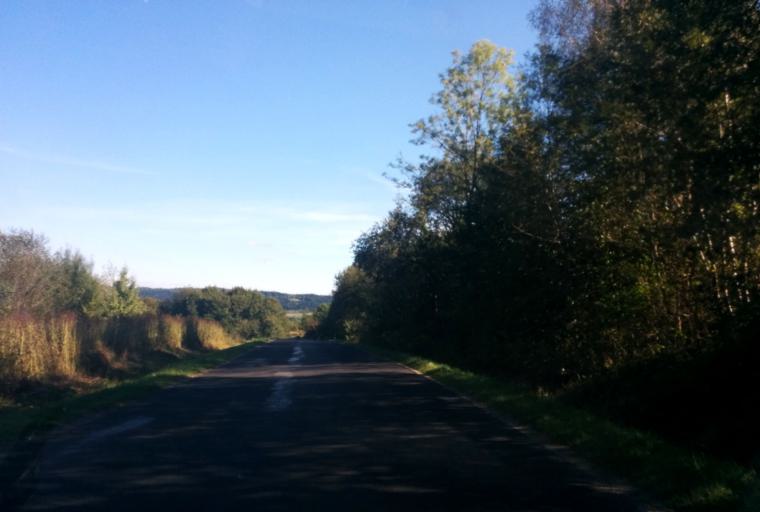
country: PL
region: Subcarpathian Voivodeship
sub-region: Powiat leski
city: Polanczyk
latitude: 49.3385
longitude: 22.4185
